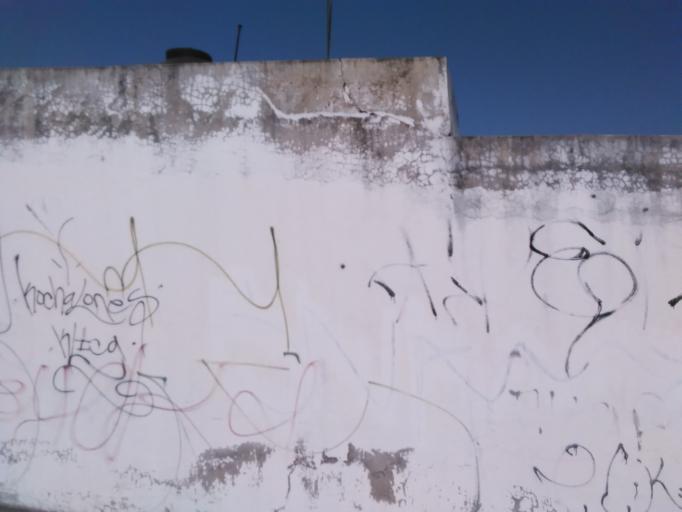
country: MX
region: Nayarit
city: Tepic
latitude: 21.4827
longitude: -104.8559
